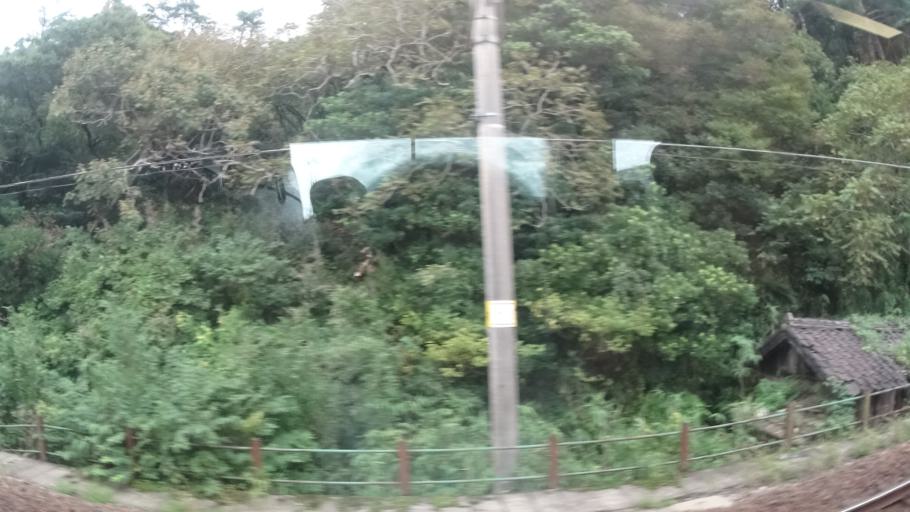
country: JP
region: Niigata
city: Murakami
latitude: 38.4112
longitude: 139.4686
